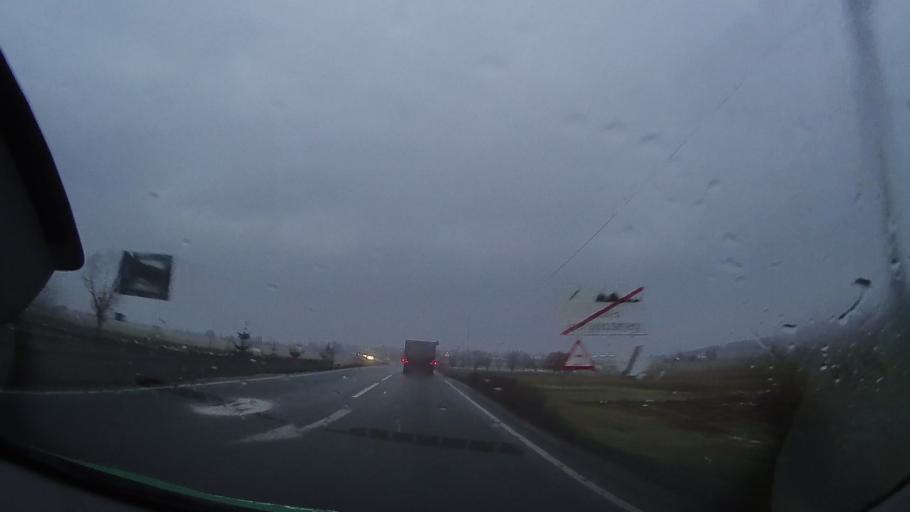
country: RO
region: Harghita
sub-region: Comuna Lazarea
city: Lazarea
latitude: 46.7587
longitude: 25.5165
